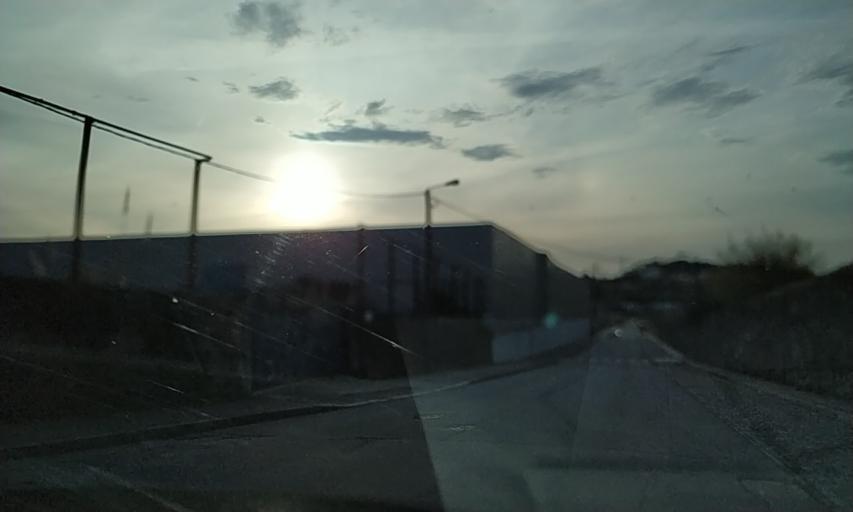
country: PT
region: Porto
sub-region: Maia
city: Leca do Bailio
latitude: 41.2045
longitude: -8.6168
